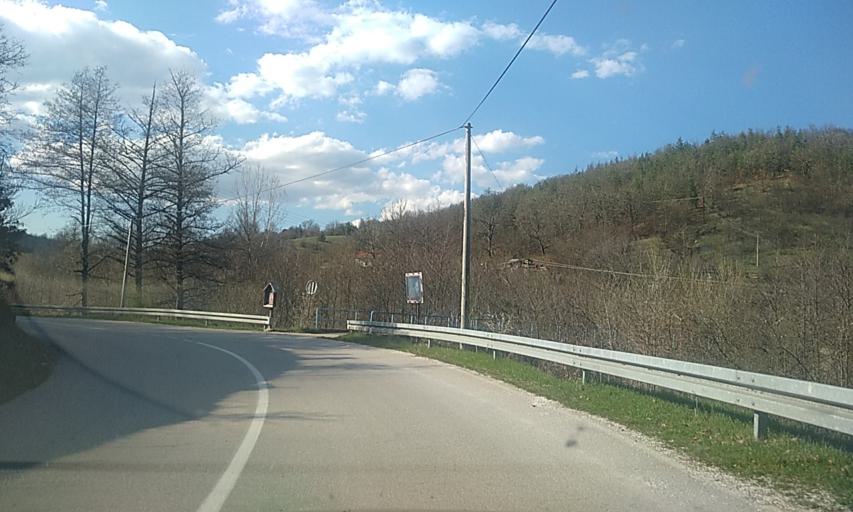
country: RS
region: Central Serbia
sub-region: Pcinjski Okrug
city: Bosilegrad
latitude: 42.4273
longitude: 22.5207
